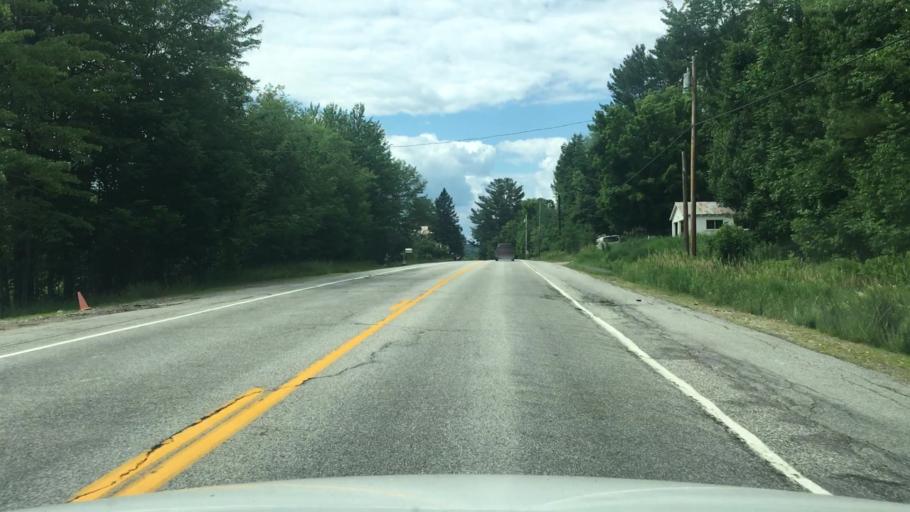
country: US
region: Maine
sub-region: Oxford County
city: West Paris
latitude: 44.3734
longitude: -70.6074
